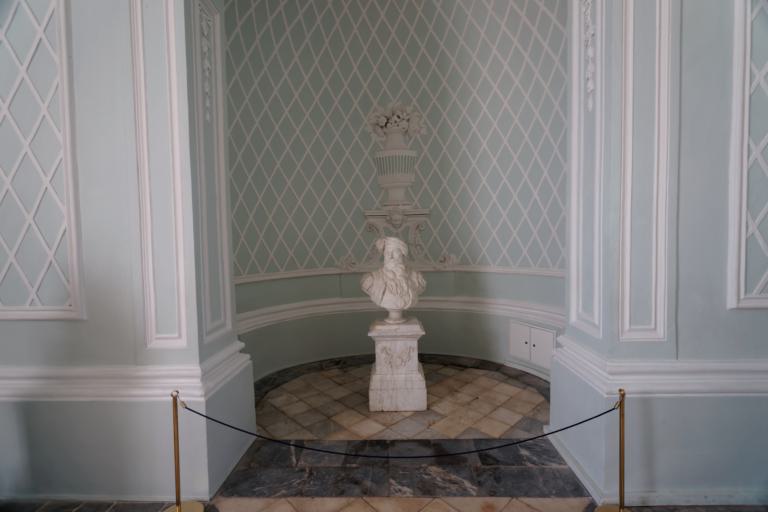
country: RU
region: St.-Petersburg
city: Pushkin
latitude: 59.7135
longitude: 30.3984
